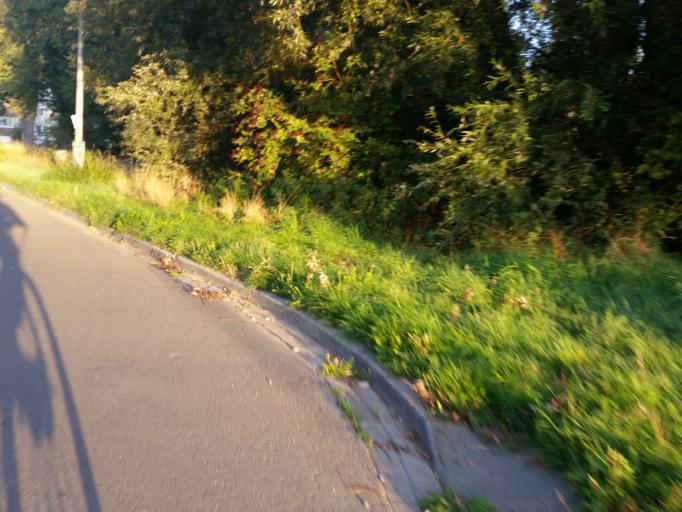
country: BE
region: Flanders
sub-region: Provincie Vlaams-Brabant
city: Vilvoorde
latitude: 50.9388
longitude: 4.4361
